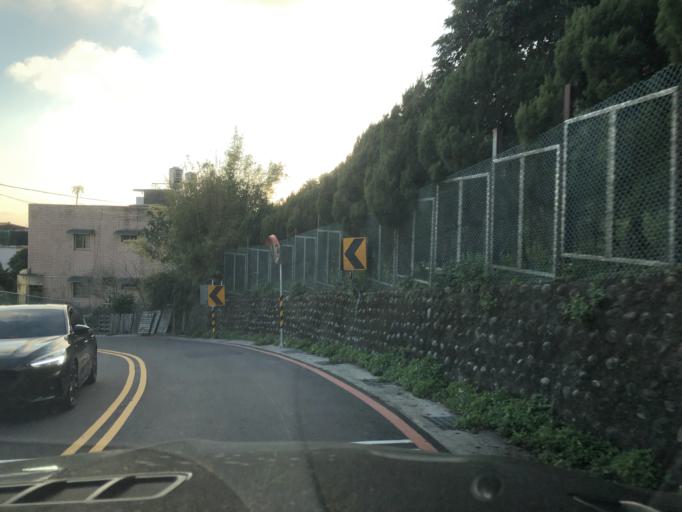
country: TW
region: Taipei
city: Taipei
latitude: 25.1458
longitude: 121.5580
